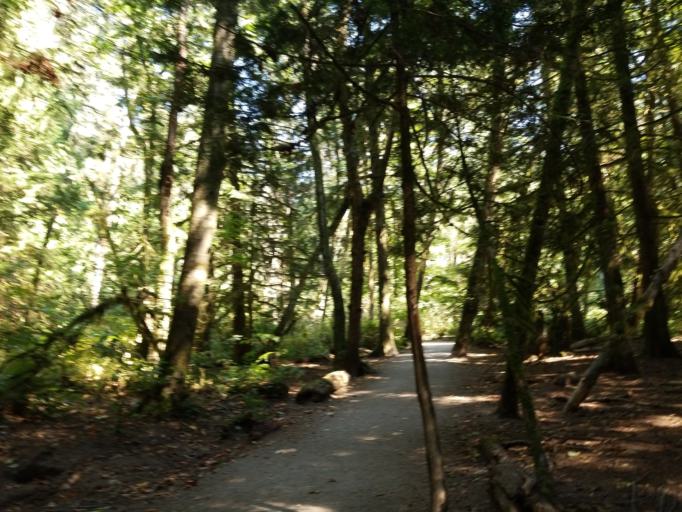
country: CA
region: British Columbia
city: West End
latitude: 49.2518
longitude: -123.2140
